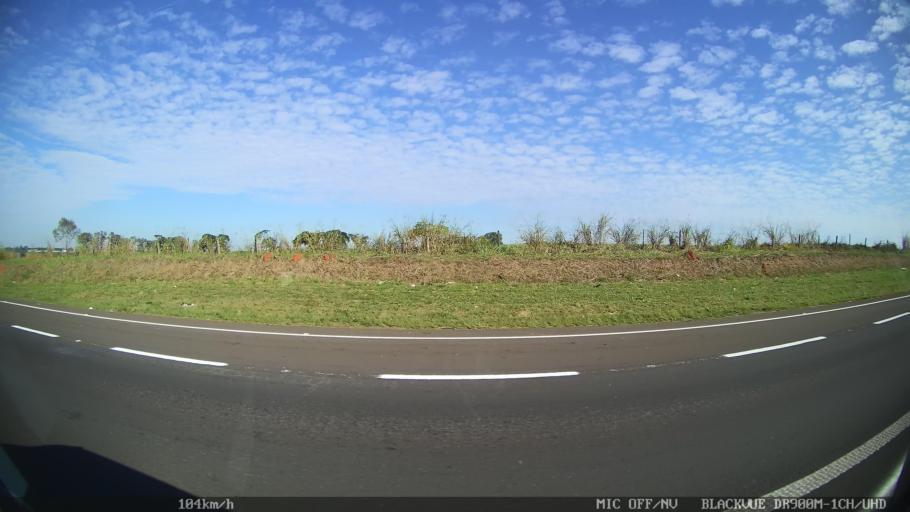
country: BR
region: Sao Paulo
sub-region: Nova Odessa
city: Nova Odessa
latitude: -22.7532
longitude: -47.2856
